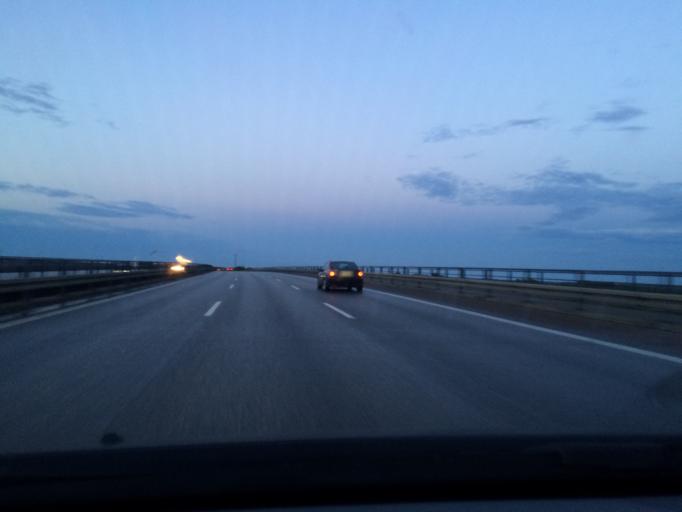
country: DK
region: Capital Region
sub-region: Hvidovre Kommune
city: Hvidovre
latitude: 55.6139
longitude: 12.5106
